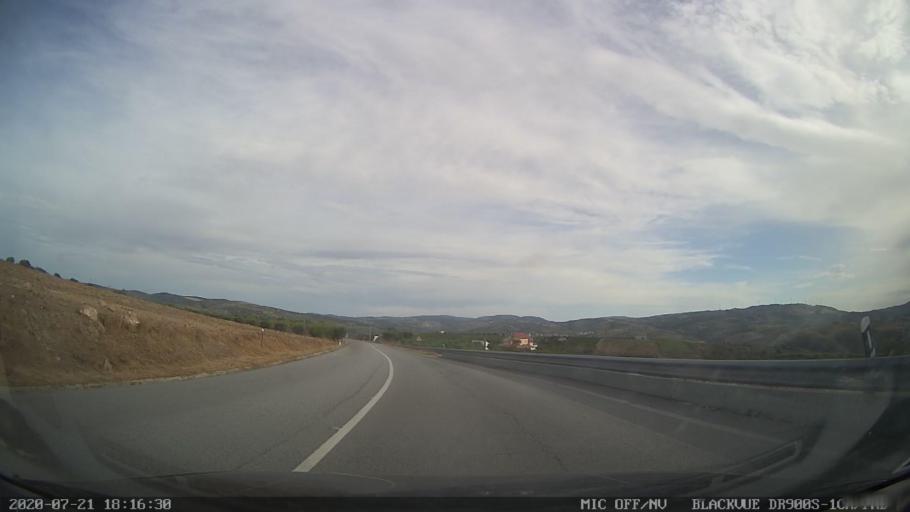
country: PT
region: Viseu
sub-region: Sao Joao da Pesqueira
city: Sao Joao da Pesqueira
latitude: 41.1085
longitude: -7.3877
